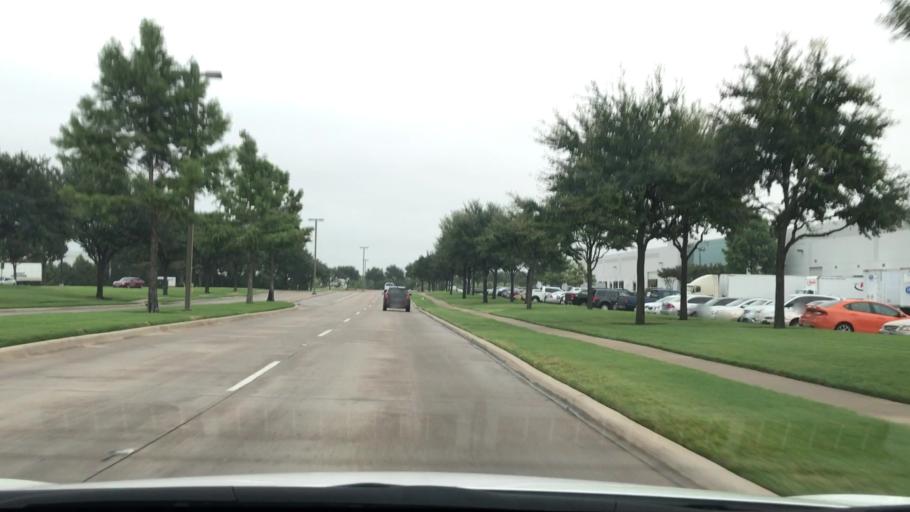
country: US
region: Texas
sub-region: Dallas County
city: Coppell
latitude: 32.9400
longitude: -97.0188
